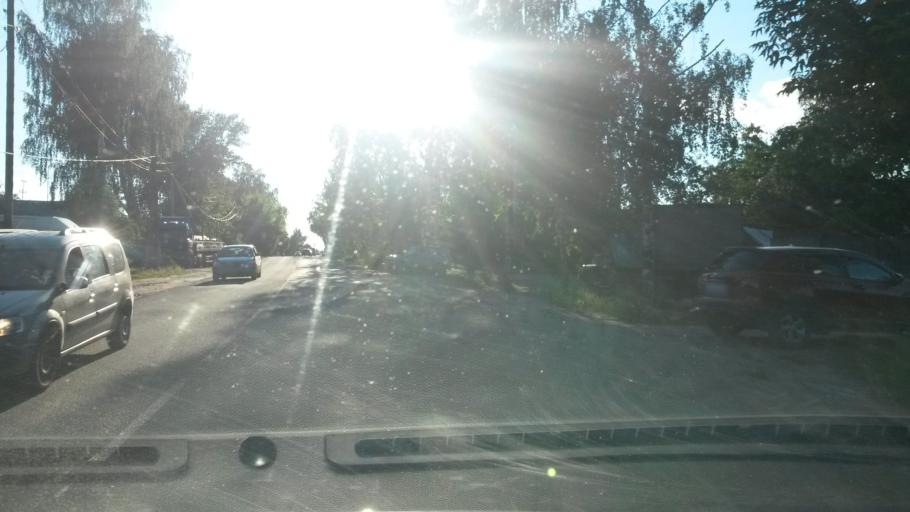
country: RU
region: Ivanovo
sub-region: Gorod Ivanovo
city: Ivanovo
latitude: 57.0202
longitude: 40.9188
